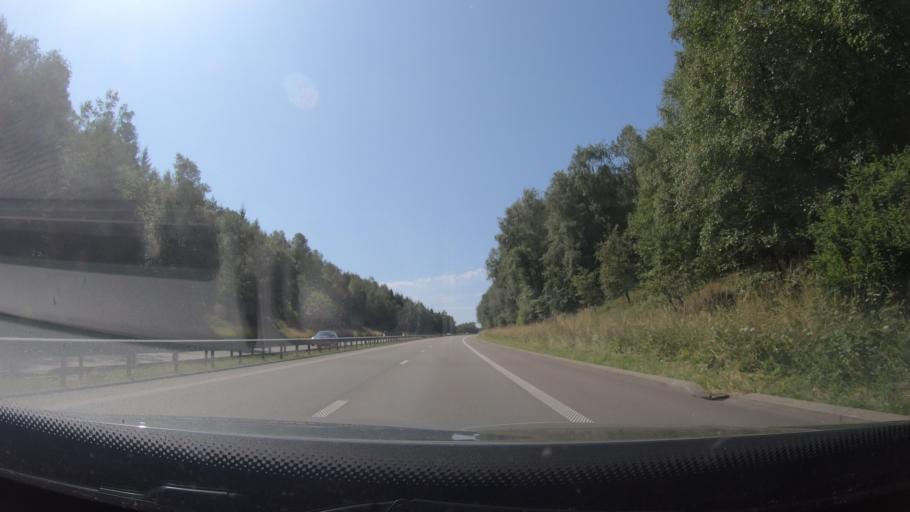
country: BE
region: Wallonia
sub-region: Province de Liege
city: Saint-Vith
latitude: 50.3360
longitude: 6.0899
